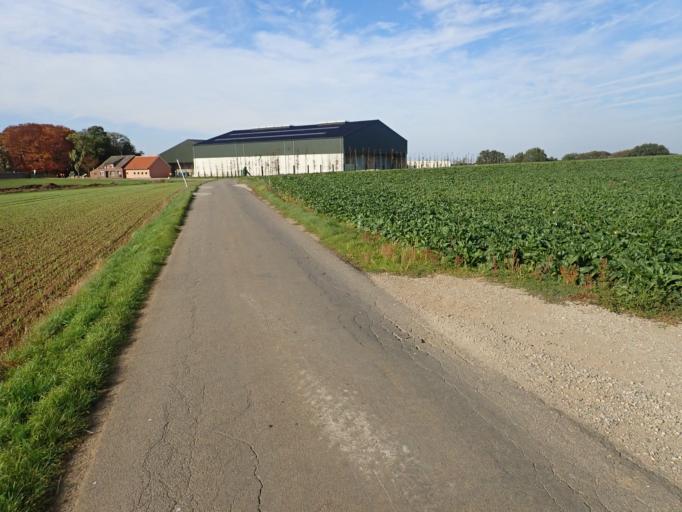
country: BE
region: Flanders
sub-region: Provincie Vlaams-Brabant
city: Diest
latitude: 50.9832
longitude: 5.0125
